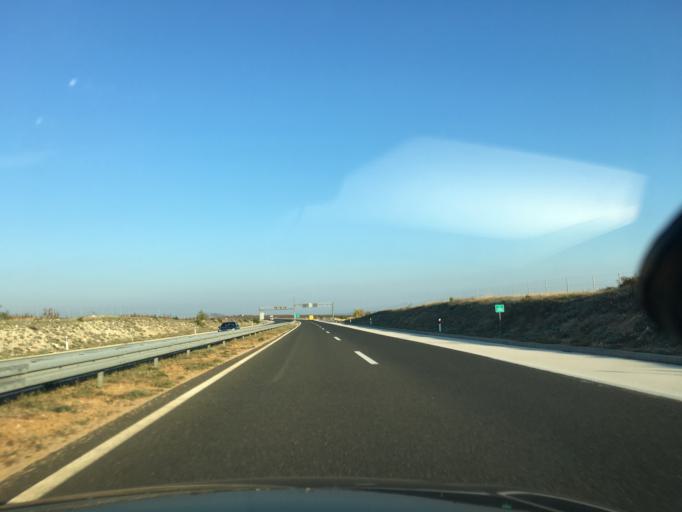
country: HR
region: Sibensko-Kniniska
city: Zaton
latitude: 43.8932
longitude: 15.7853
